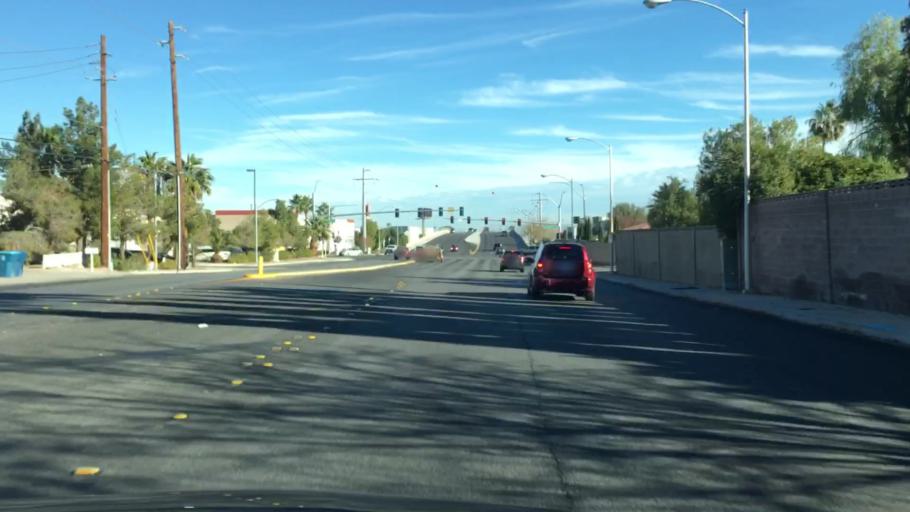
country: US
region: Nevada
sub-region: Clark County
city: Paradise
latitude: 36.0571
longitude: -115.1851
